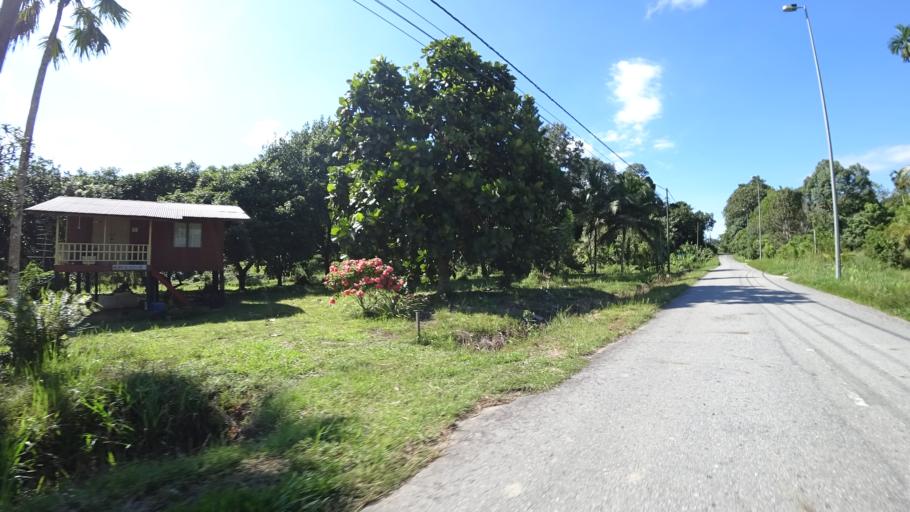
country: BN
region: Tutong
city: Tutong
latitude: 4.7479
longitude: 114.7842
